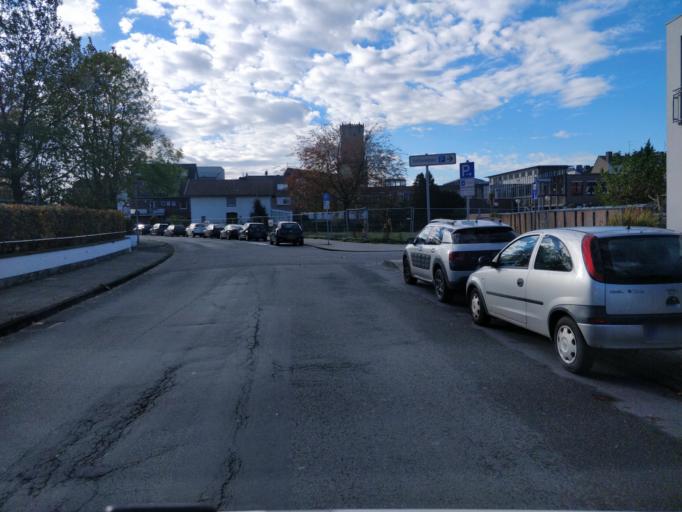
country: DE
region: North Rhine-Westphalia
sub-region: Regierungsbezirk Dusseldorf
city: Emmerich
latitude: 51.8319
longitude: 6.2475
